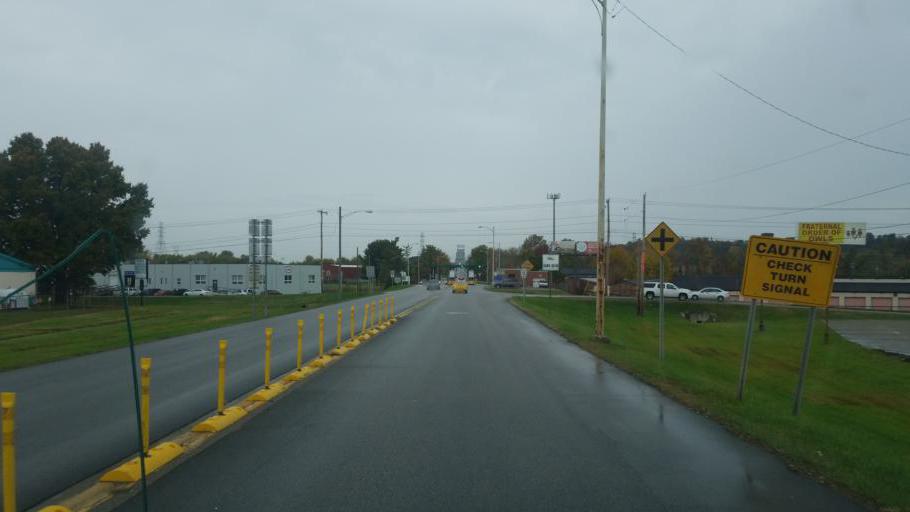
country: US
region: West Virginia
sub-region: Wood County
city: Parkersburg
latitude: 39.2827
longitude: -81.5510
